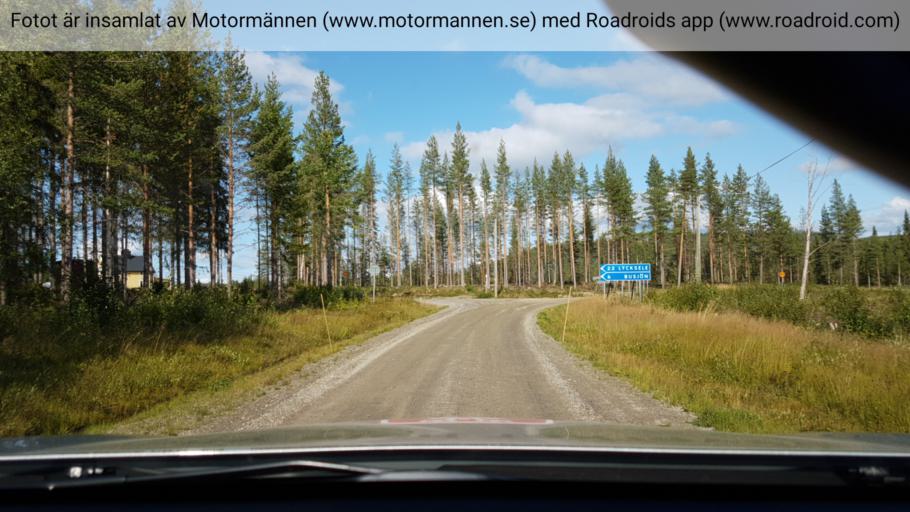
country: SE
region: Vaesterbotten
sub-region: Lycksele Kommun
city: Lycksele
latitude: 64.5798
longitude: 19.0190
